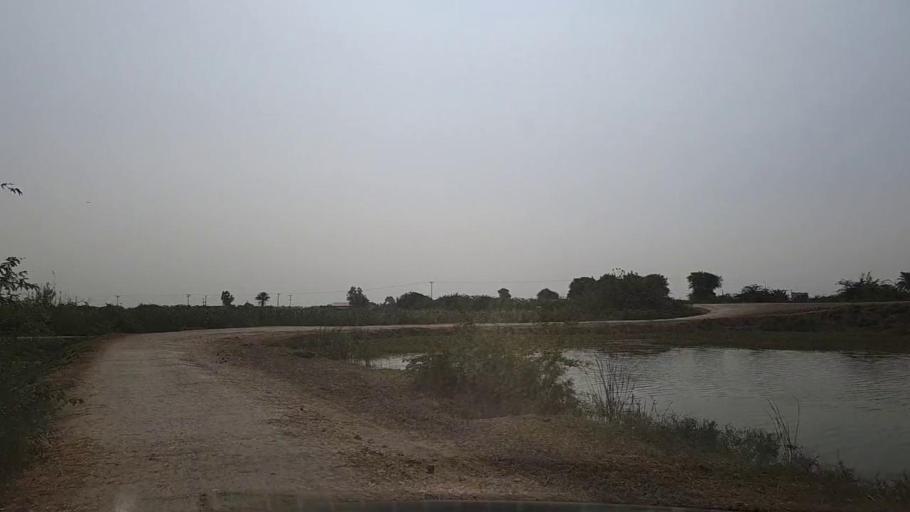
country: PK
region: Sindh
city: Chuhar Jamali
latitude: 24.5428
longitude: 67.9129
